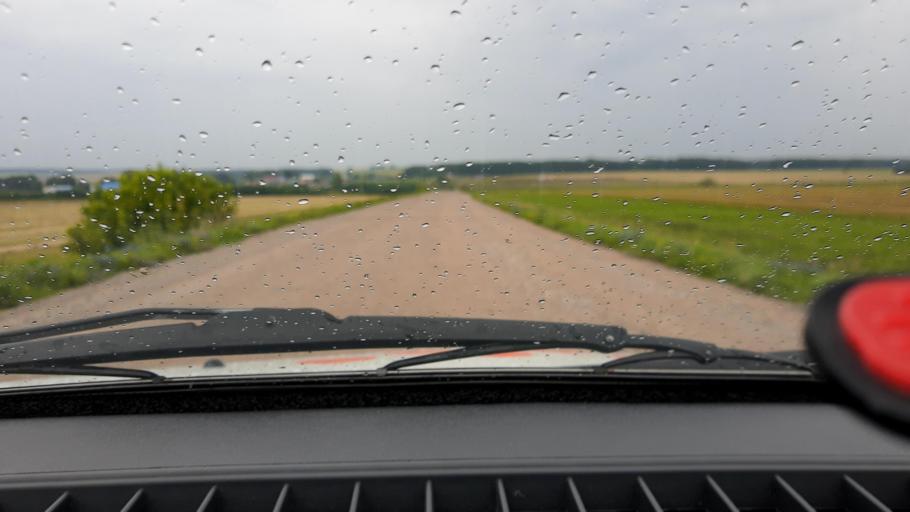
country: RU
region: Bashkortostan
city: Karmaskaly
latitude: 54.3866
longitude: 56.1225
